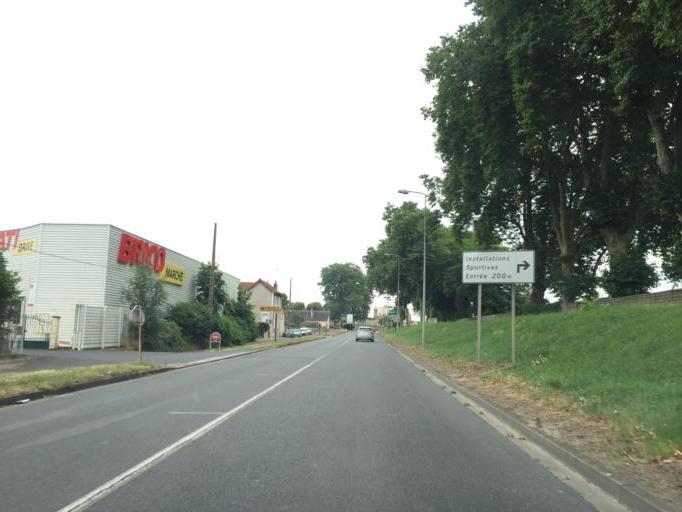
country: FR
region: Auvergne
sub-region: Departement de l'Allier
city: Moulins
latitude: 46.5700
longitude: 3.3215
